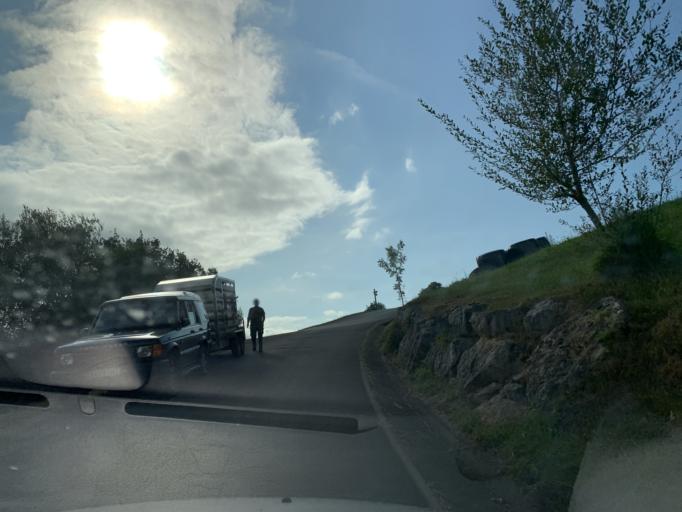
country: ES
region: Asturias
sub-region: Province of Asturias
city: Carrena
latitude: 43.3266
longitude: -4.8611
